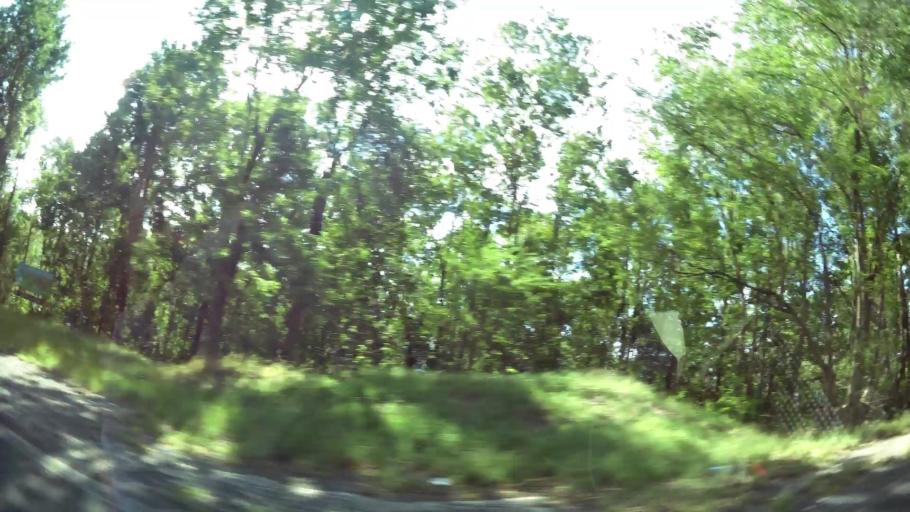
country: GP
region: Guadeloupe
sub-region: Guadeloupe
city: Sainte-Rose
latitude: 16.3251
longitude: -61.7861
